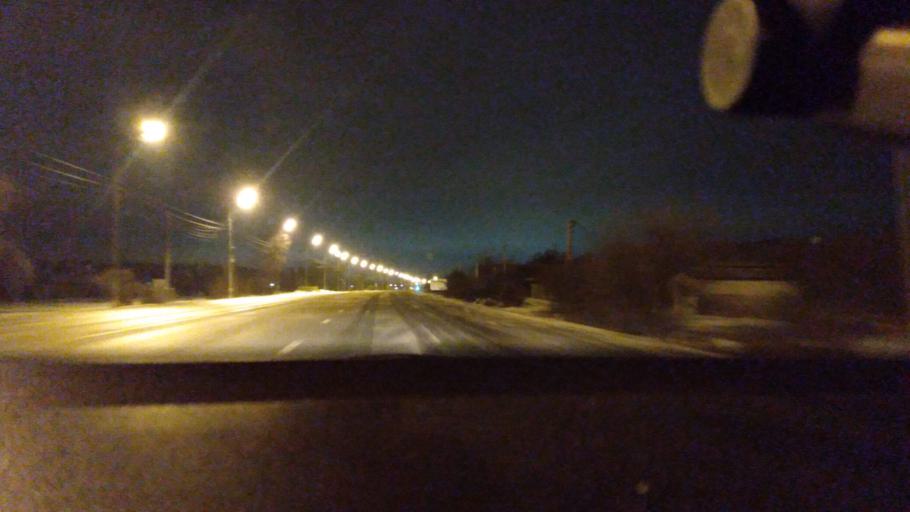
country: RU
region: Moskovskaya
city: Bronnitsy
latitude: 55.3988
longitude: 38.3136
